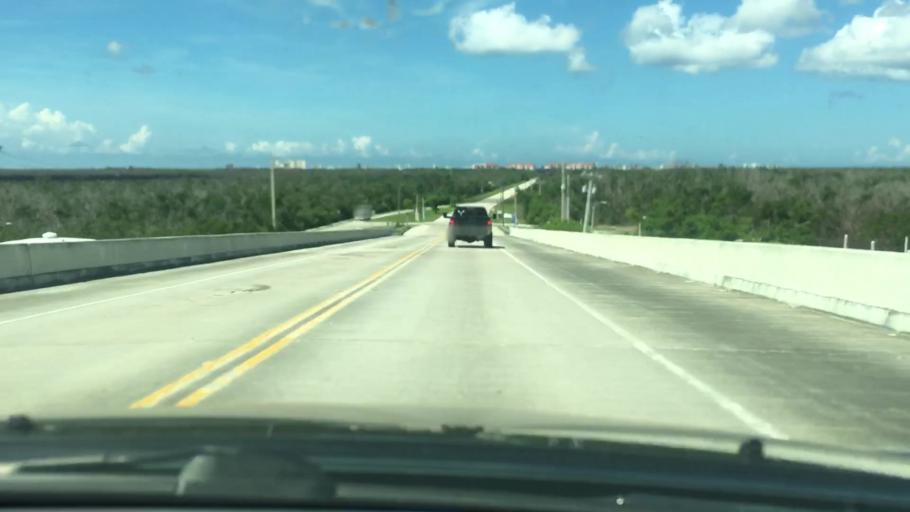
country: US
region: Florida
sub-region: Collier County
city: Marco
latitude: 25.9326
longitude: -81.6549
